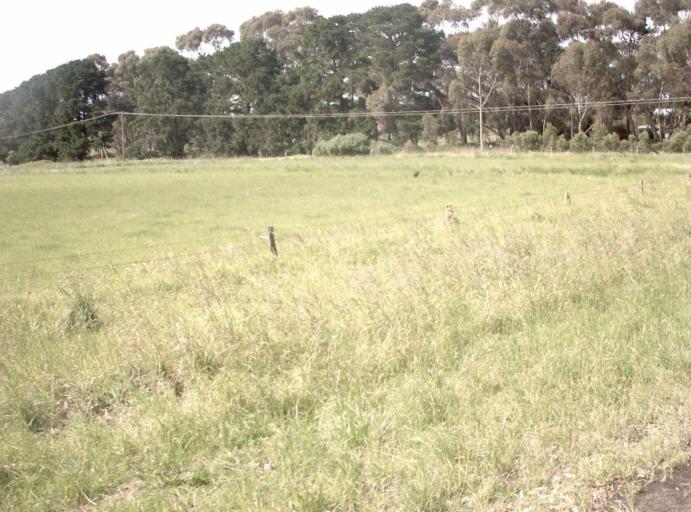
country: AU
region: Victoria
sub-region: Bass Coast
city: Phillip Island
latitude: -38.4716
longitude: 145.1882
